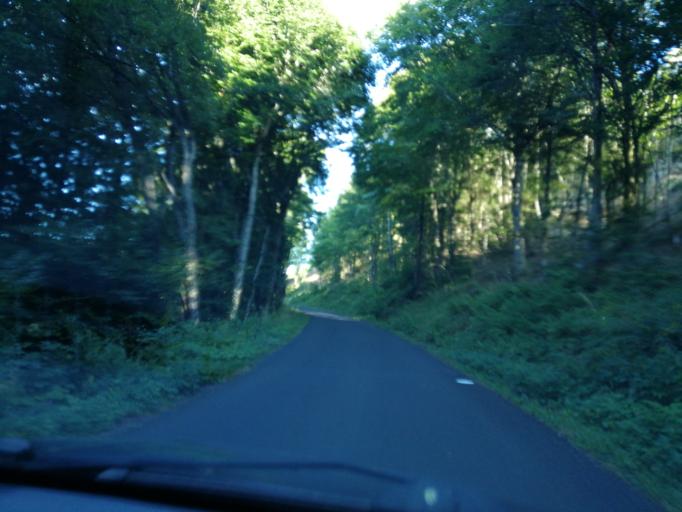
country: FR
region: Auvergne
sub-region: Departement du Cantal
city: Vic-sur-Cere
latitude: 45.0768
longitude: 2.5666
